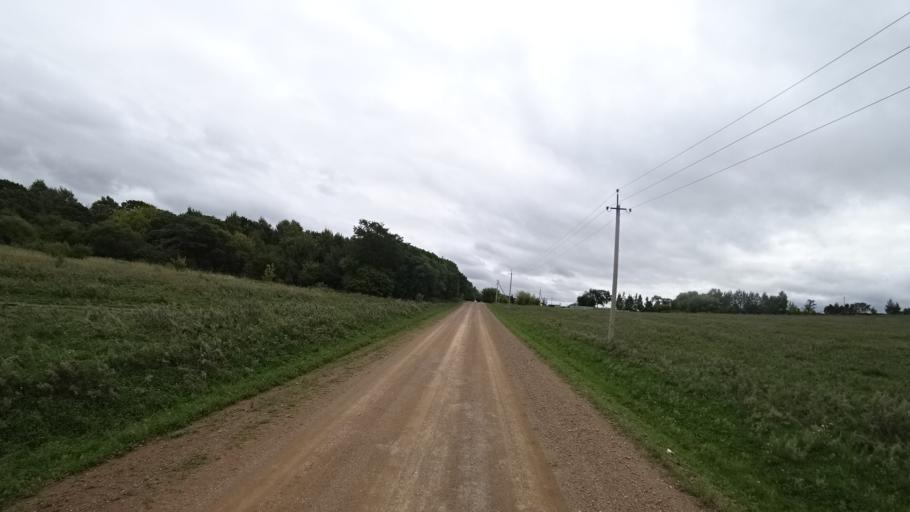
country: RU
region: Primorskiy
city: Chernigovka
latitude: 44.4648
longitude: 132.5892
